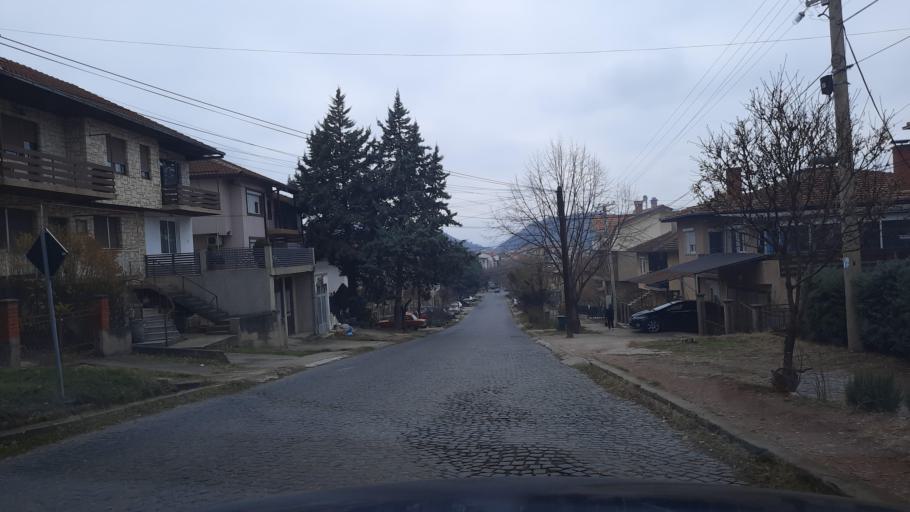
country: MK
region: Stip
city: Shtip
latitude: 41.7456
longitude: 22.2020
